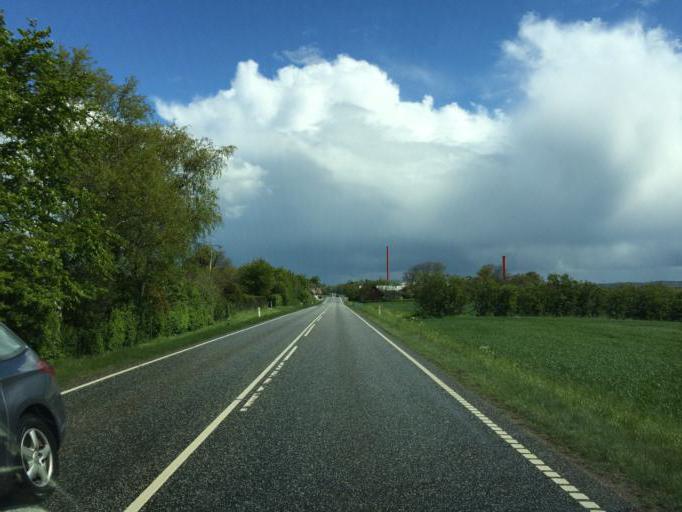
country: DK
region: Central Jutland
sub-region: Holstebro Kommune
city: Holstebro
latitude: 56.4174
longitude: 8.6986
